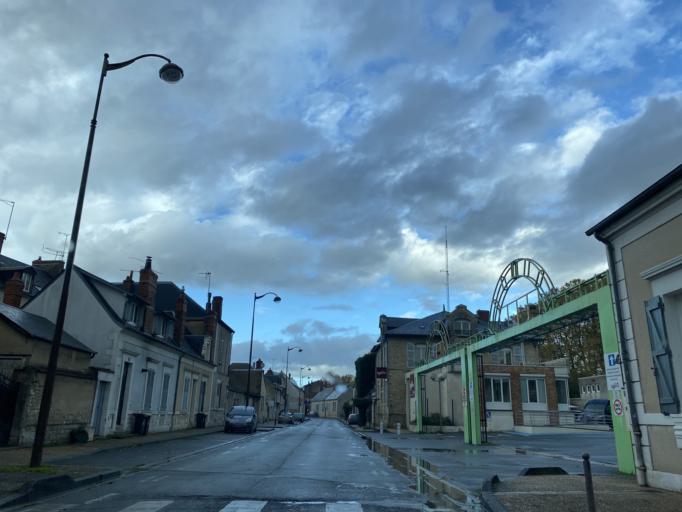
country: FR
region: Centre
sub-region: Departement du Cher
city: Bourges
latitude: 47.0756
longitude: 2.3903
